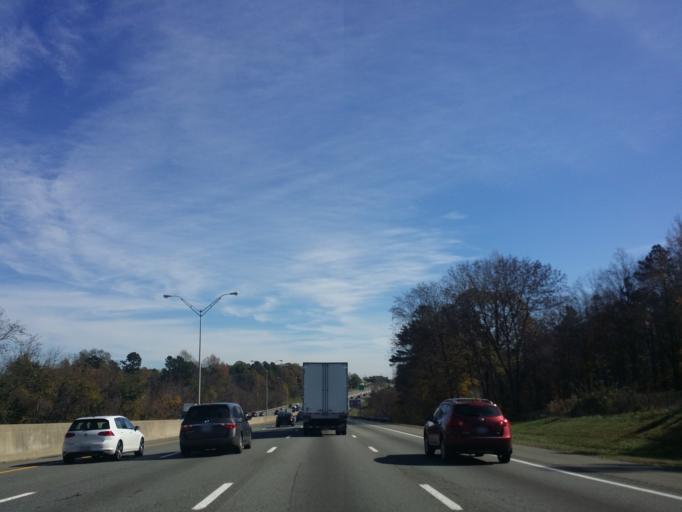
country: US
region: North Carolina
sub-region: Alamance County
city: Graham
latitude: 36.0628
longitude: -79.4190
